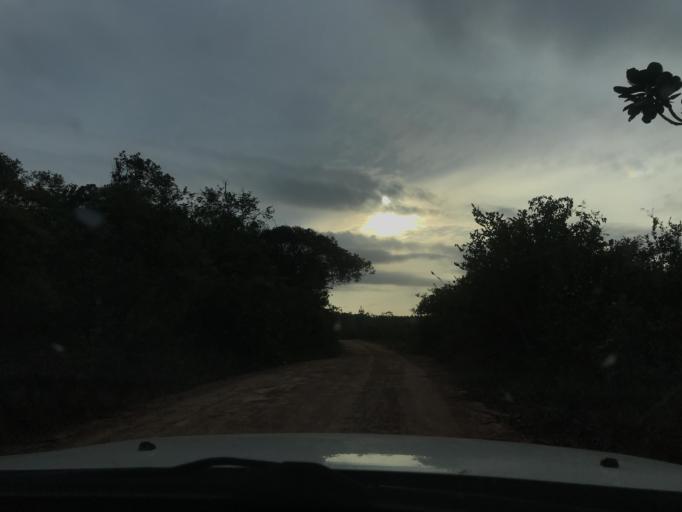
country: BR
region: Bahia
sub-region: Entre Rios
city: Entre Rios
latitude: -12.0526
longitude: -38.2226
